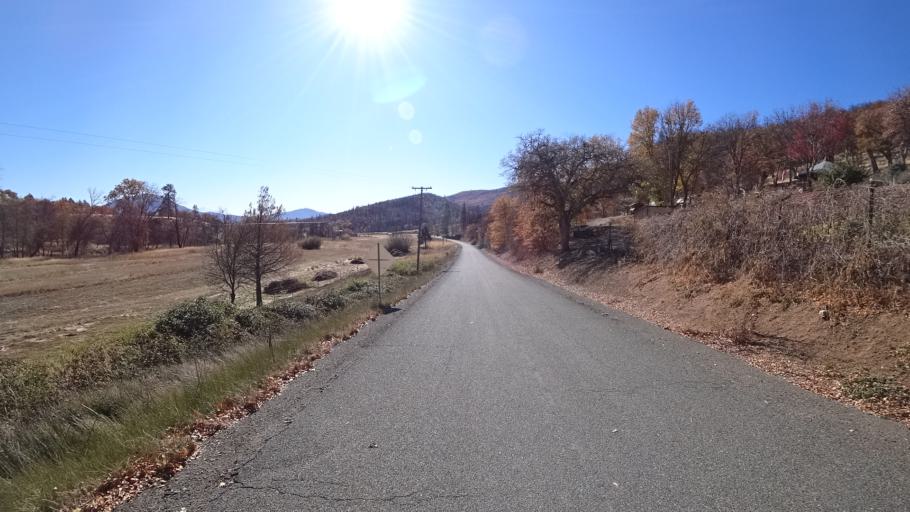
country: US
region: California
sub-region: Siskiyou County
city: Yreka
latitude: 41.9399
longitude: -122.5915
